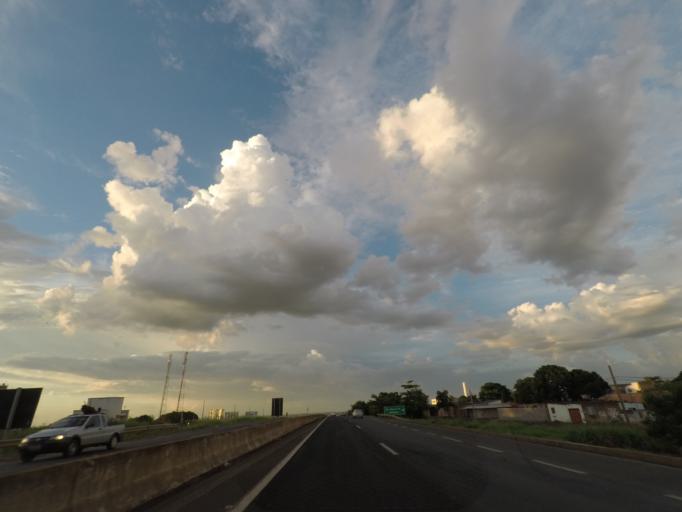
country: BR
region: Minas Gerais
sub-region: Uberaba
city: Uberaba
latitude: -19.7740
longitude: -47.9725
